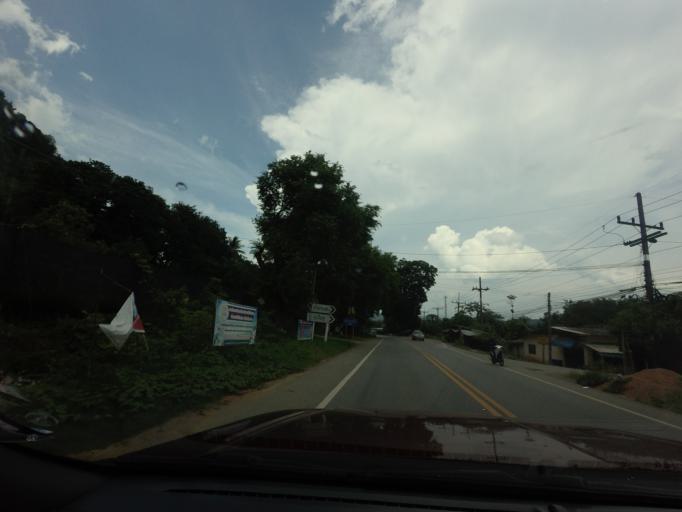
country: TH
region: Yala
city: Ban Nang Sata
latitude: 6.2339
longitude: 101.2108
